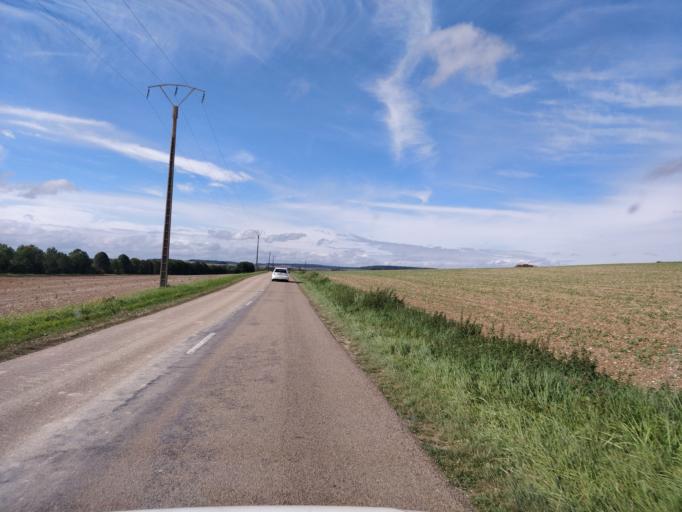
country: FR
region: Champagne-Ardenne
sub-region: Departement de l'Aube
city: Aix-en-Othe
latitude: 48.2170
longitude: 3.6222
